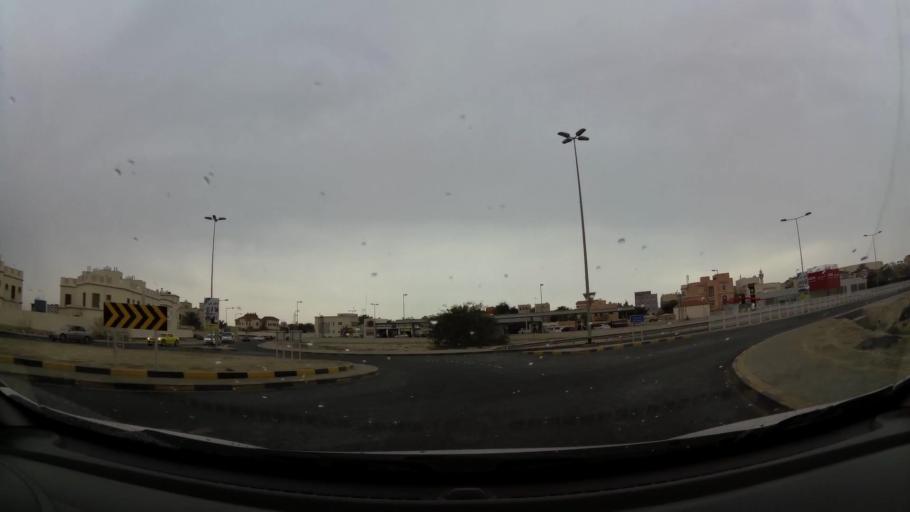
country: BH
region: Central Governorate
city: Madinat Hamad
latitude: 26.1323
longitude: 50.4936
